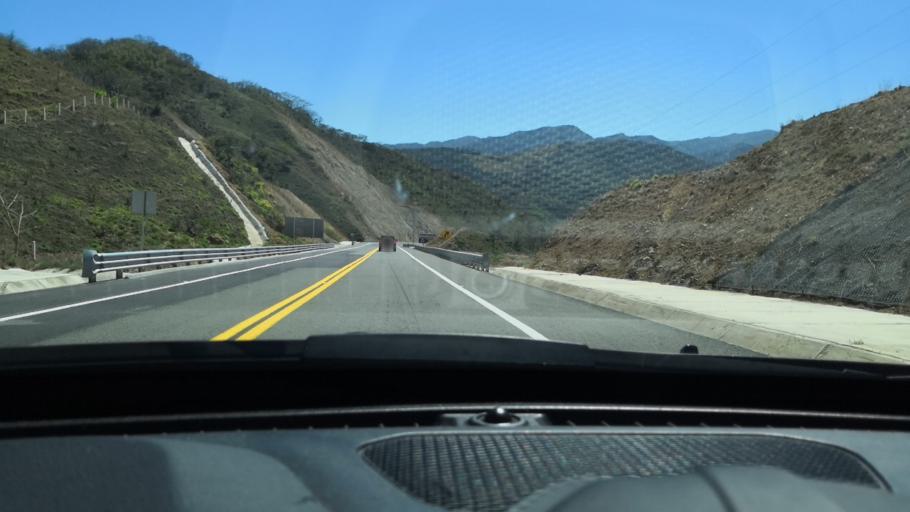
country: MX
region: Nayarit
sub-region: Compostela
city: Juan Escutia (Borbollon)
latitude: 21.1435
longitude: -104.9098
